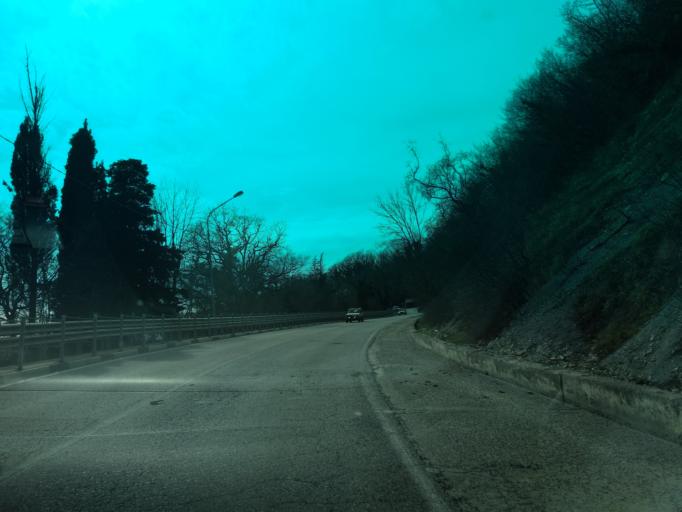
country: RU
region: Krasnodarskiy
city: Shepsi
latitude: 44.0407
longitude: 39.1468
